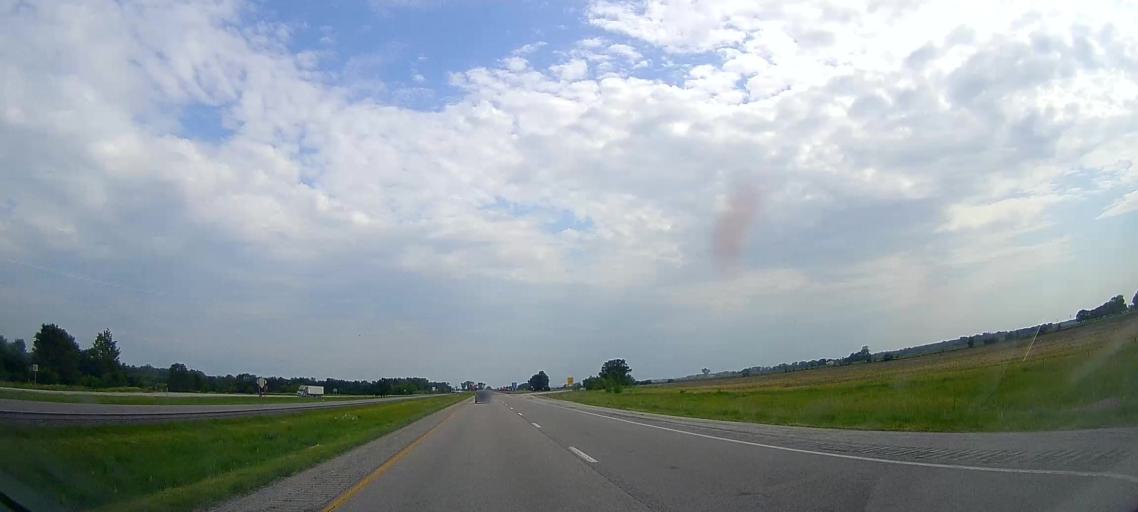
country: US
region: Nebraska
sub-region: Burt County
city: Tekamah
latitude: 41.7456
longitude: -96.0473
